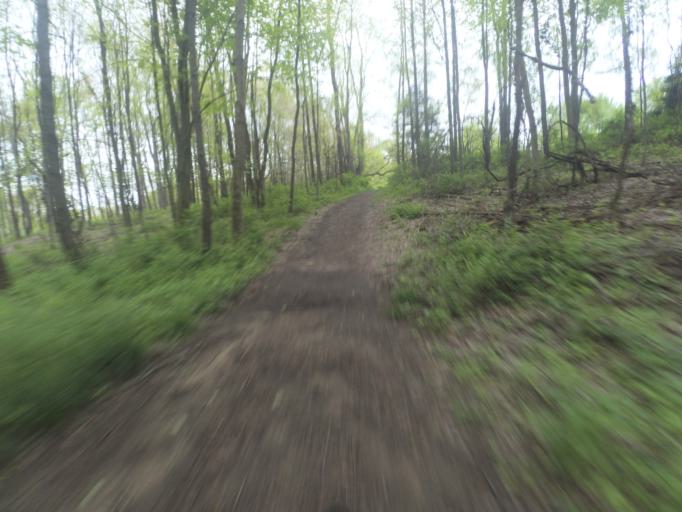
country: US
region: Ohio
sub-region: Portage County
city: Ravenna
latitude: 41.1722
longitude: -81.3005
